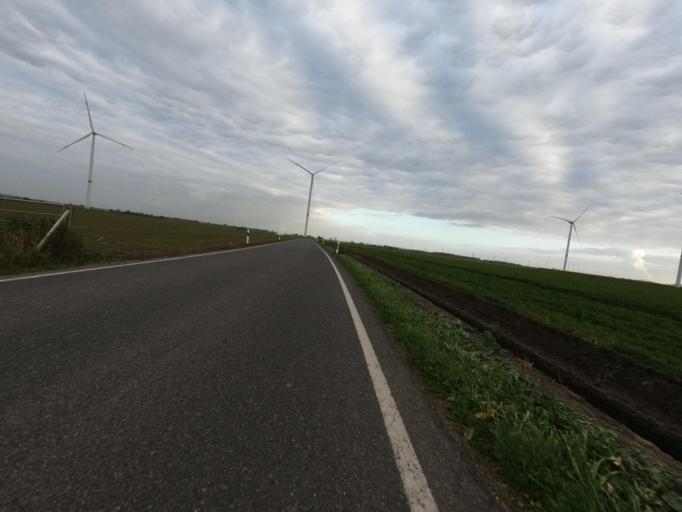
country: DE
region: North Rhine-Westphalia
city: Geilenkirchen
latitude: 51.0196
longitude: 6.1495
